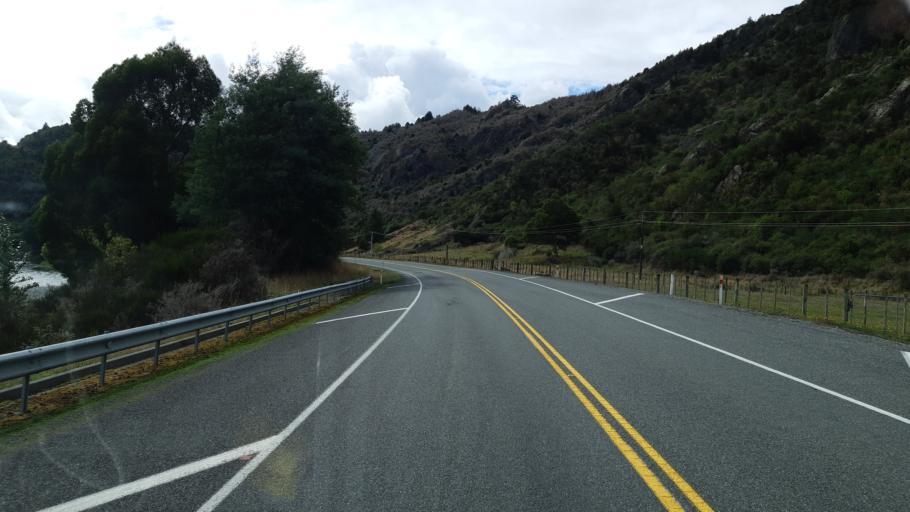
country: NZ
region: West Coast
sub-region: Buller District
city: Westport
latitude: -41.7971
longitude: 172.3596
